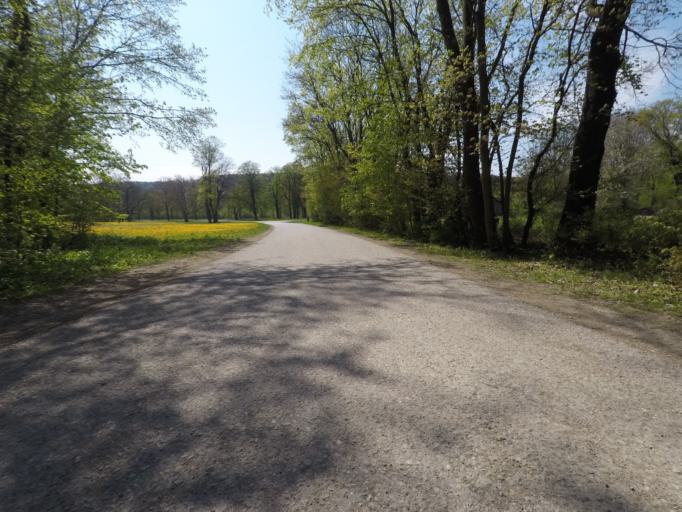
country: AT
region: Lower Austria
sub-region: Politischer Bezirk Modling
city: Perchtoldsdorf
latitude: 48.1688
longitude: 16.2447
